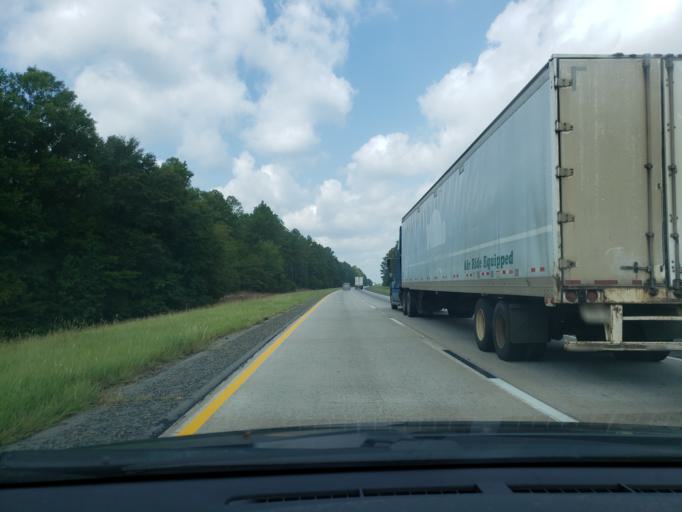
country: US
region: Georgia
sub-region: Treutlen County
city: Soperton
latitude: 32.4266
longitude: -82.5480
